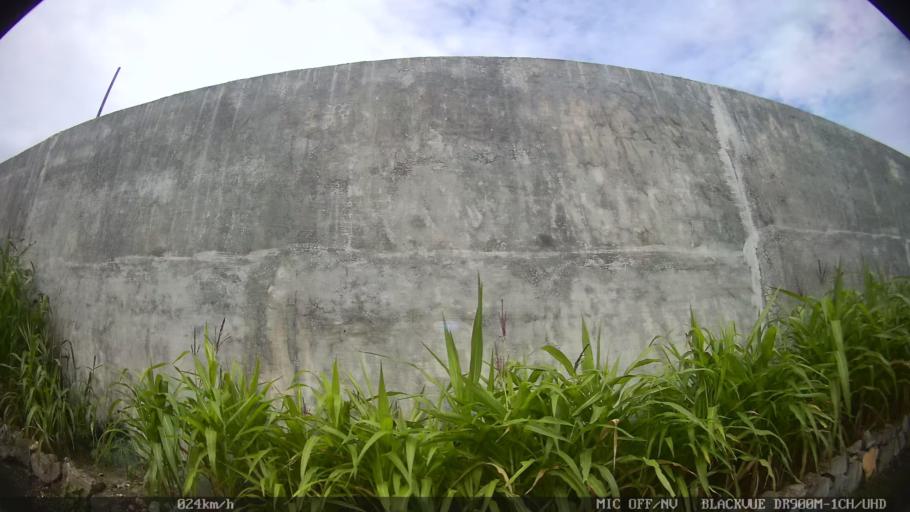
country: ID
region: North Sumatra
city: Sunggal
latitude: 3.5976
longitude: 98.5832
